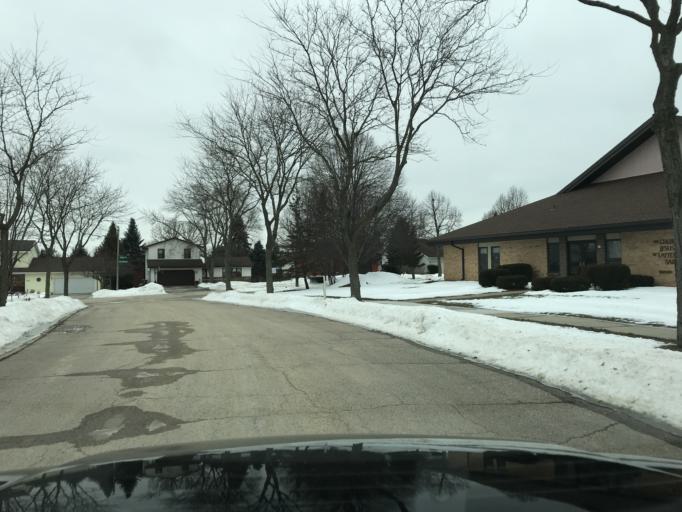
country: US
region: Wisconsin
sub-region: Dane County
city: Monona
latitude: 43.0710
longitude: -89.2844
